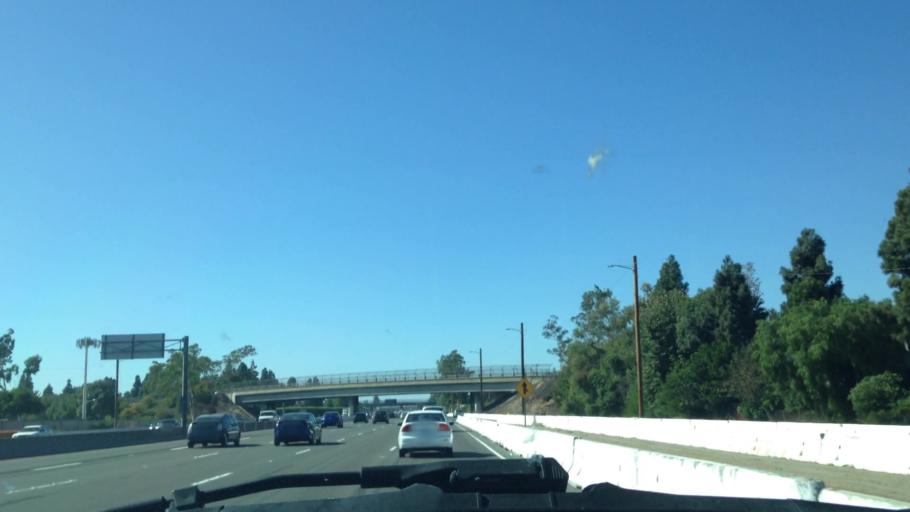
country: US
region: California
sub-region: Orange County
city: Fountain Valley
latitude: 33.7077
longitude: -117.9556
